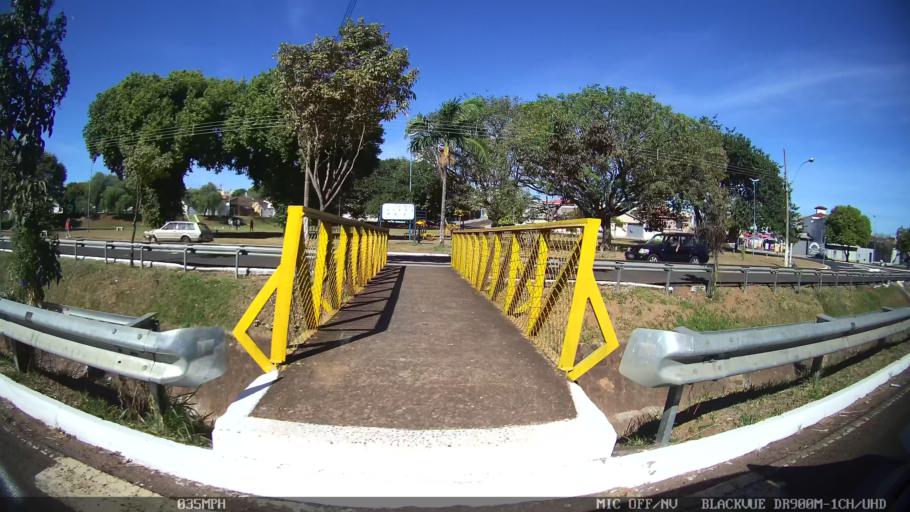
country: BR
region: Sao Paulo
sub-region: Franca
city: Franca
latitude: -20.5198
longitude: -47.3900
